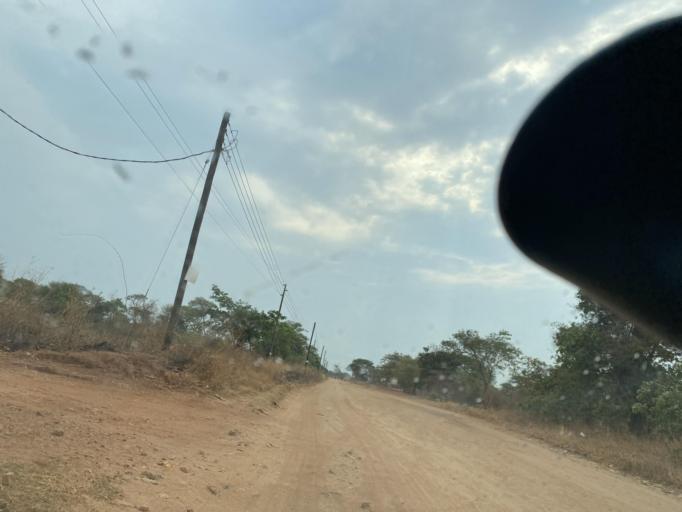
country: ZM
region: Lusaka
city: Lusaka
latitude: -15.2897
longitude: 28.2808
